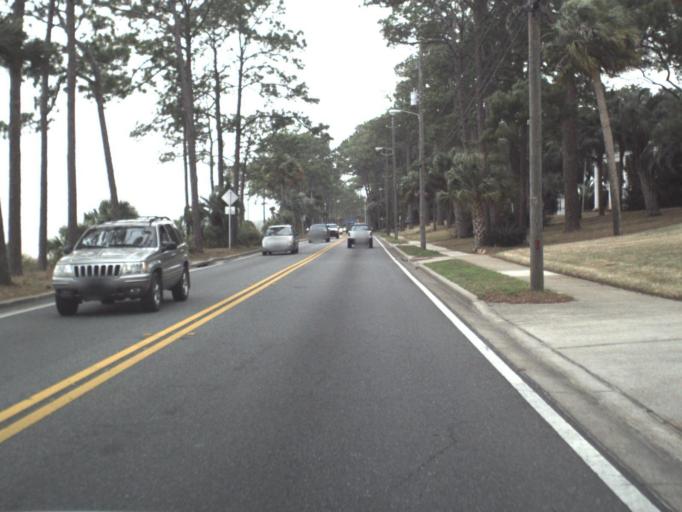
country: US
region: Florida
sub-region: Bay County
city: Panama City
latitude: 30.1608
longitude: -85.6736
